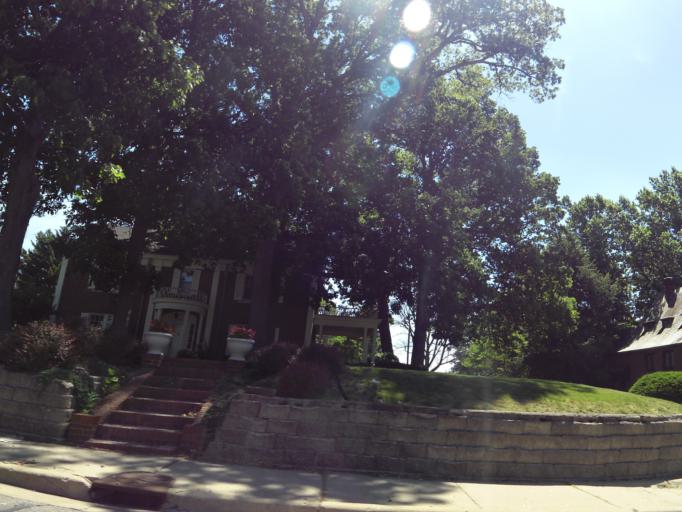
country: US
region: Illinois
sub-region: Vermilion County
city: Danville
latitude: 40.1552
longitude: -87.6303
